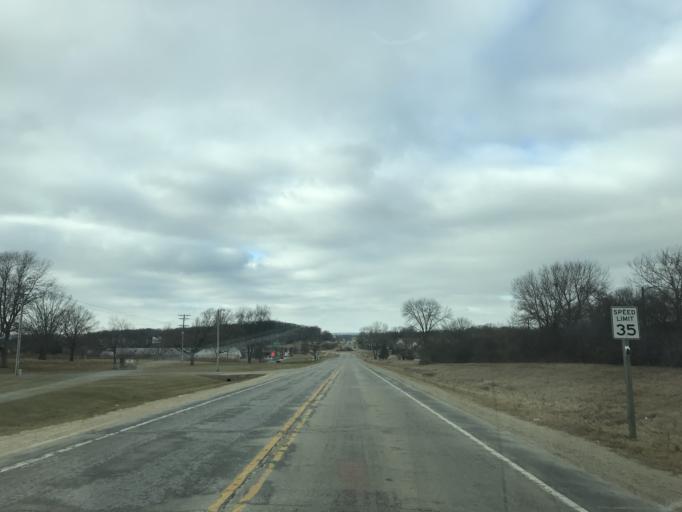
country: US
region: Wisconsin
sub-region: Dane County
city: Monona
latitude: 43.1065
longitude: -89.2933
